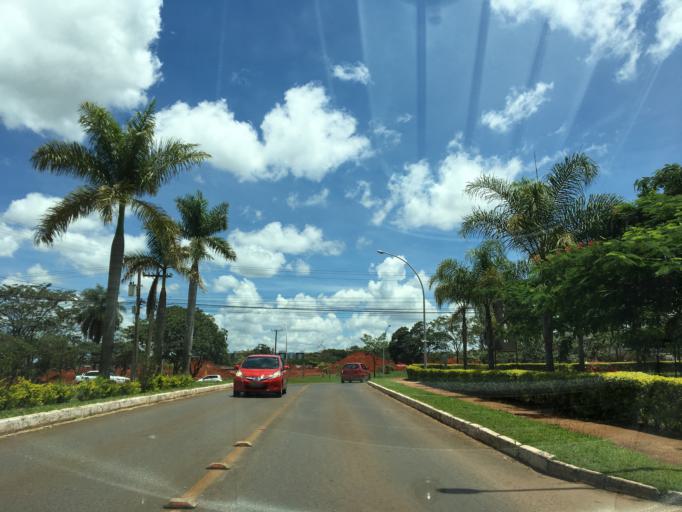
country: BR
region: Federal District
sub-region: Brasilia
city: Brasilia
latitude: -15.7318
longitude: -47.8960
